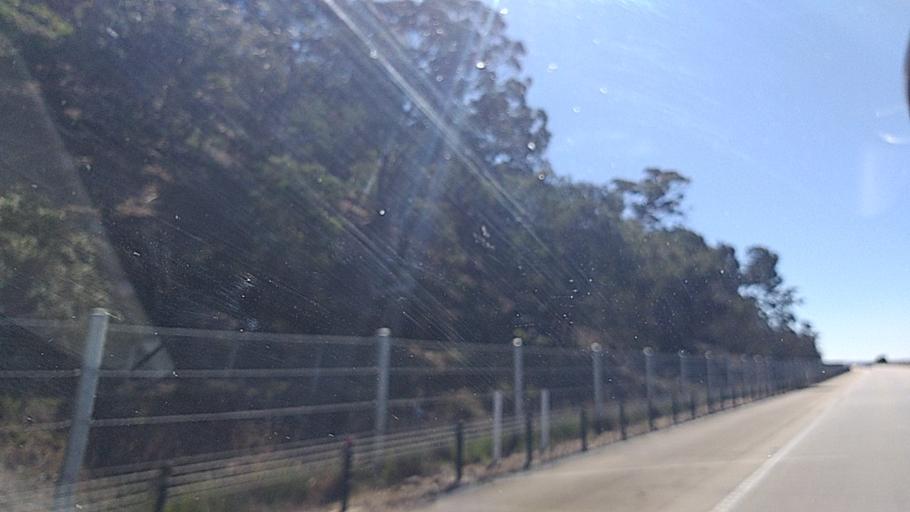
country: AU
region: New South Wales
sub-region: Yass Valley
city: Gundaroo
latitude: -35.0608
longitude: 149.3738
